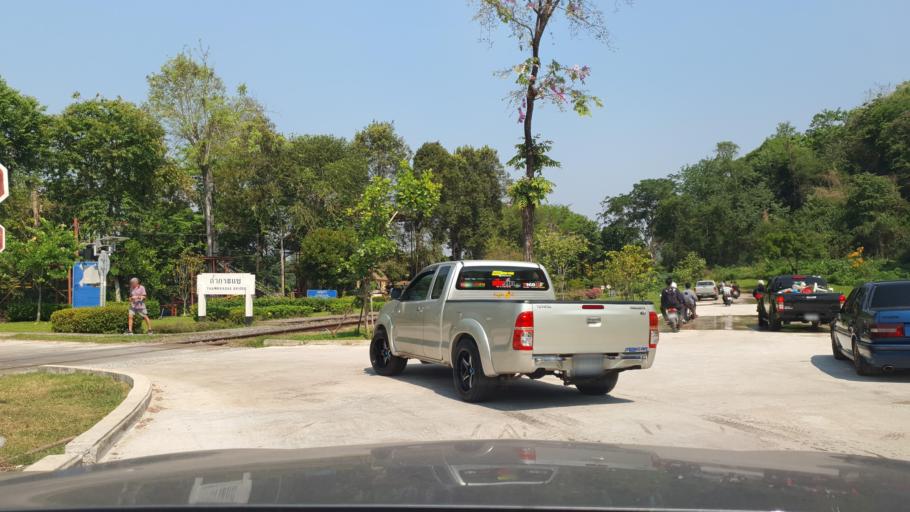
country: TH
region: Kanchanaburi
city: Sai Yok
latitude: 14.0997
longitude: 99.1701
